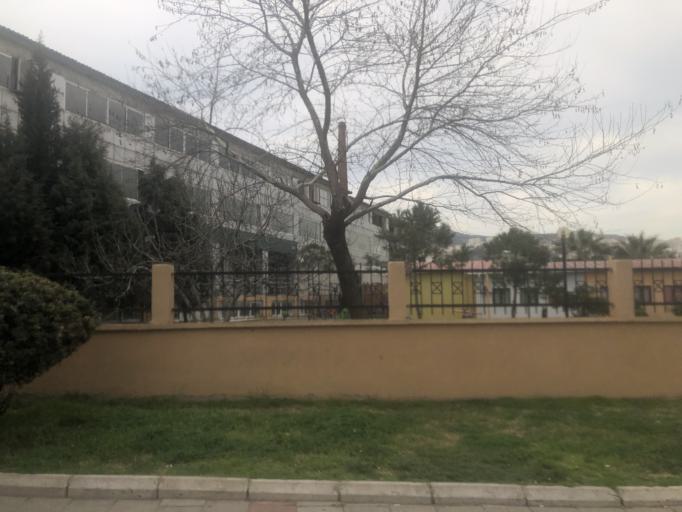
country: TR
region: Izmir
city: Karsiyaka
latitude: 38.4903
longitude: 27.0683
